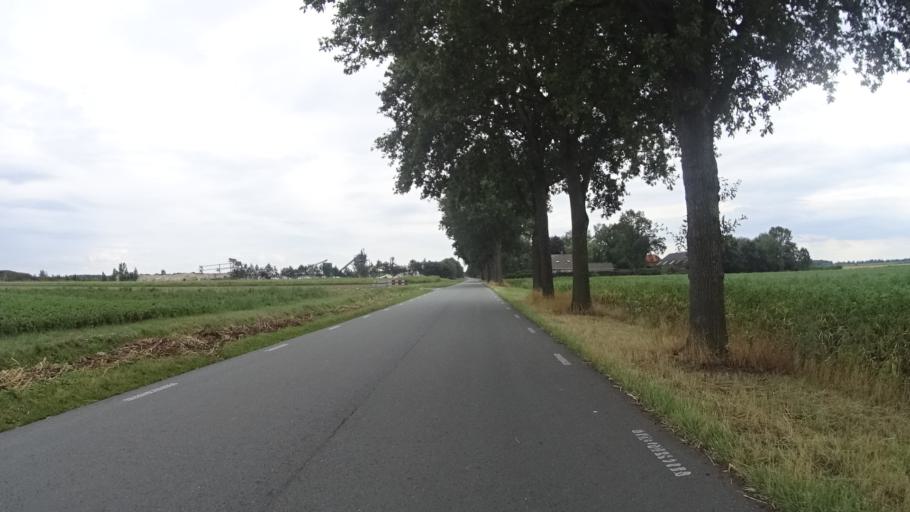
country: NL
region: Groningen
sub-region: Gemeente Slochteren
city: Slochteren
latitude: 53.1889
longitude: 6.8507
